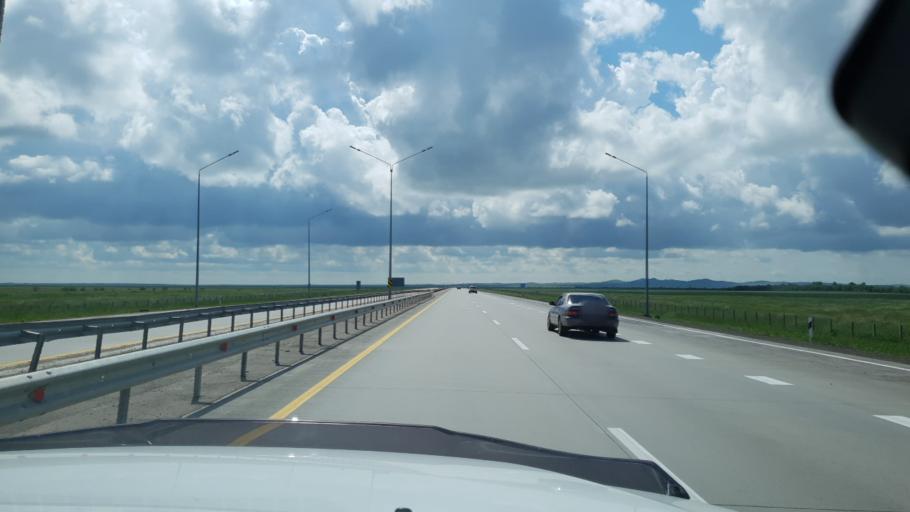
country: KZ
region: Qaraghandy
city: Osakarovka
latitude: 50.6549
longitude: 72.4166
